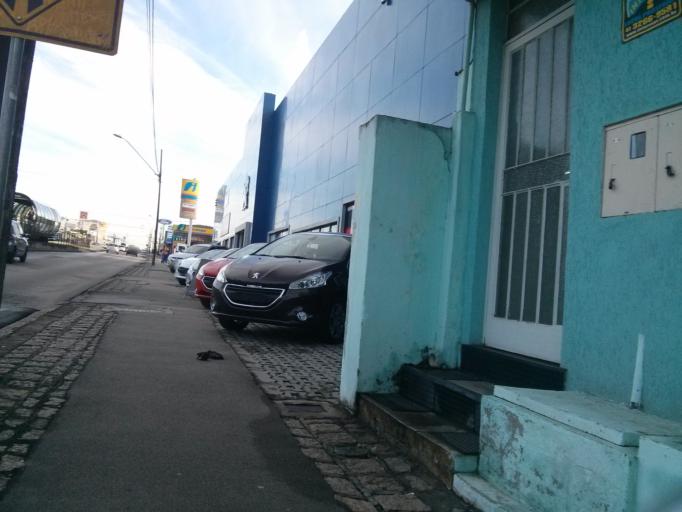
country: BR
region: Parana
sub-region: Curitiba
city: Curitiba
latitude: -25.4633
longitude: -49.2560
